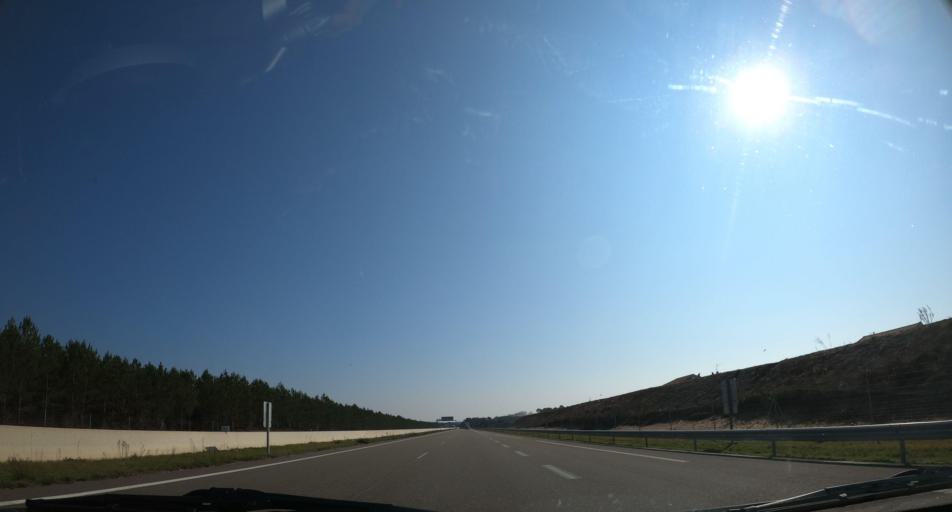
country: FR
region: Aquitaine
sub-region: Departement des Landes
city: Saint-Geours-de-Maremne
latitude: 43.6961
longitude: -1.2217
